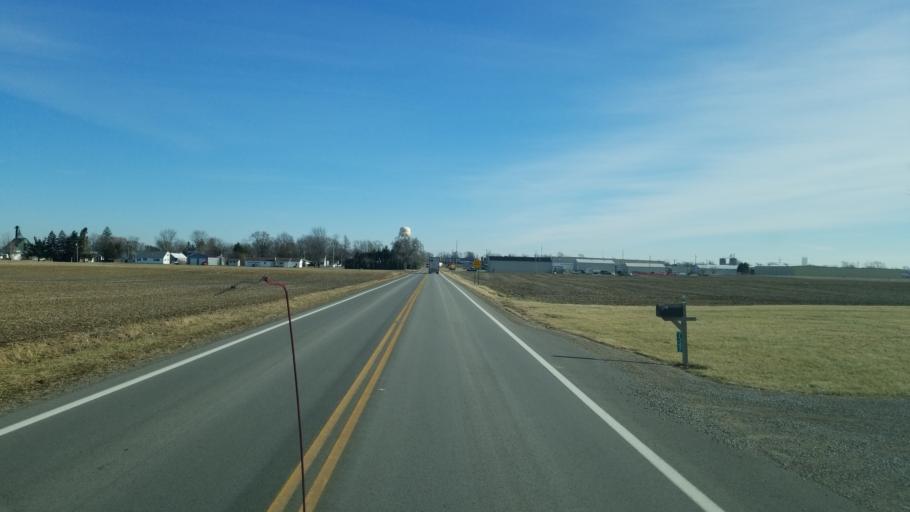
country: US
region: Ohio
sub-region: Putnam County
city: Leipsic
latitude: 41.1016
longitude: -84.0031
